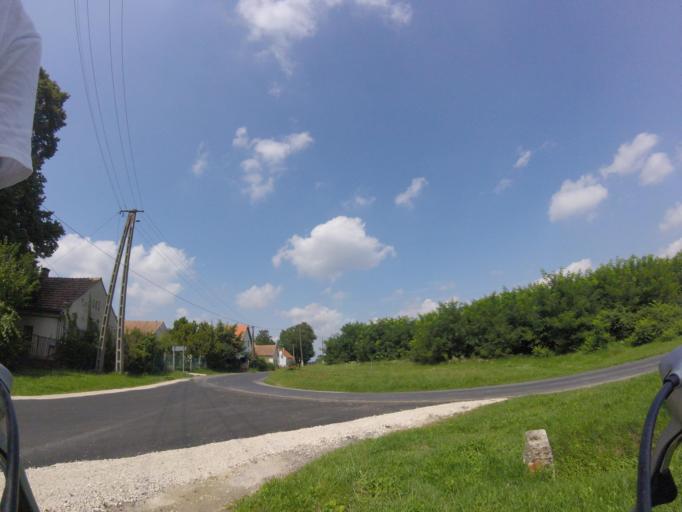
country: HU
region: Zala
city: Zalakomar
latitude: 46.5413
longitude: 17.2718
